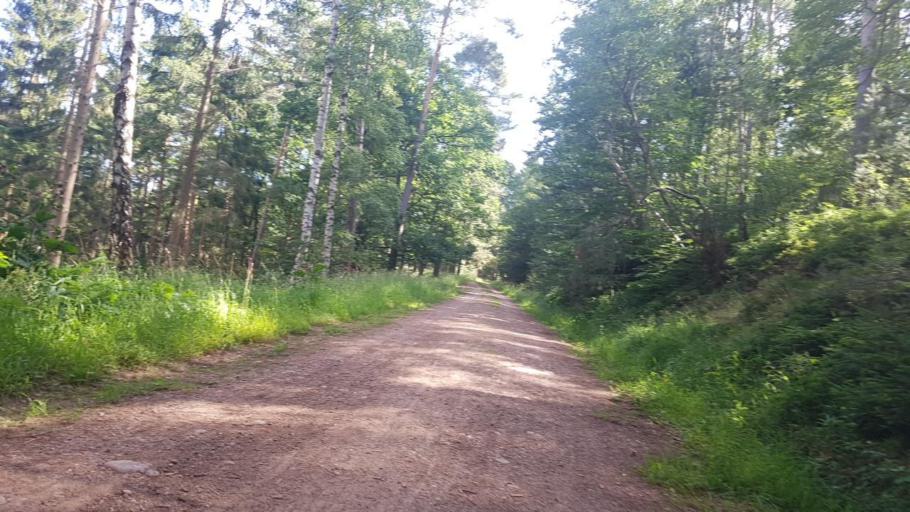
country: DE
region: North Rhine-Westphalia
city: Heimbach
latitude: 50.6182
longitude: 6.5070
